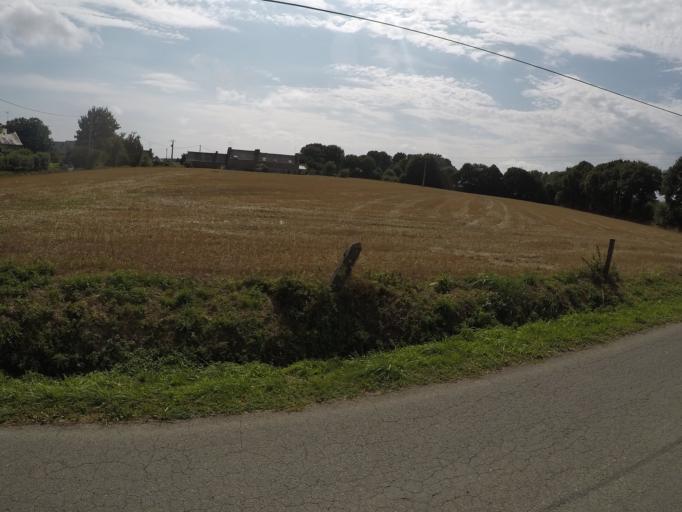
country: FR
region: Brittany
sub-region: Departement des Cotes-d'Armor
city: Goudelin
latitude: 48.6032
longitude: -3.0088
